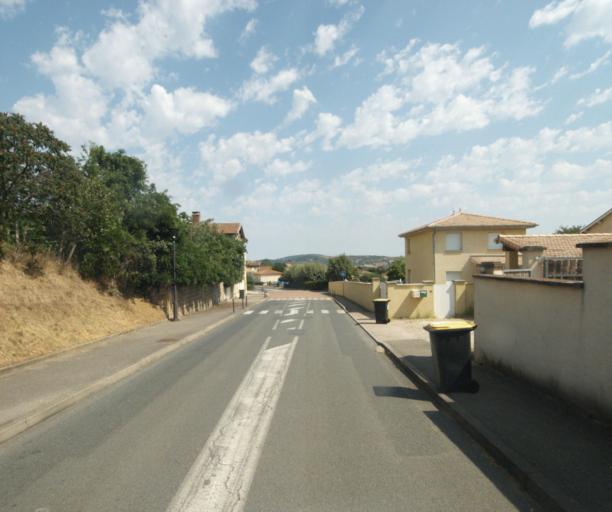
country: FR
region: Rhone-Alpes
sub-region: Departement du Rhone
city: Lentilly
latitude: 45.8372
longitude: 4.6529
